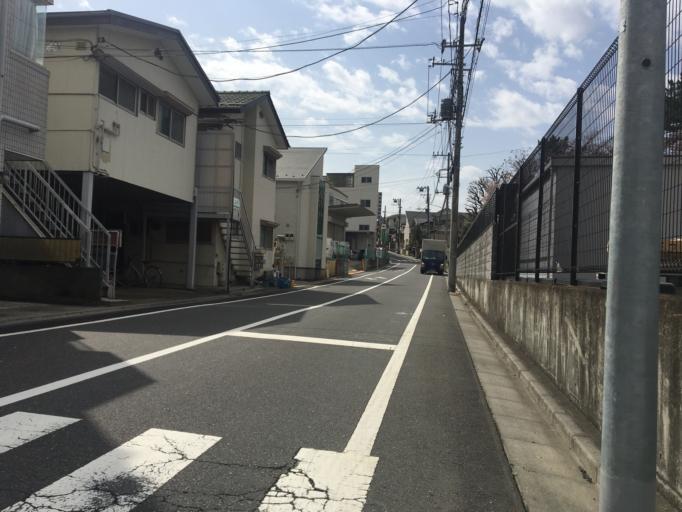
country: JP
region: Saitama
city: Shimotoda
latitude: 35.7516
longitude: 139.6779
